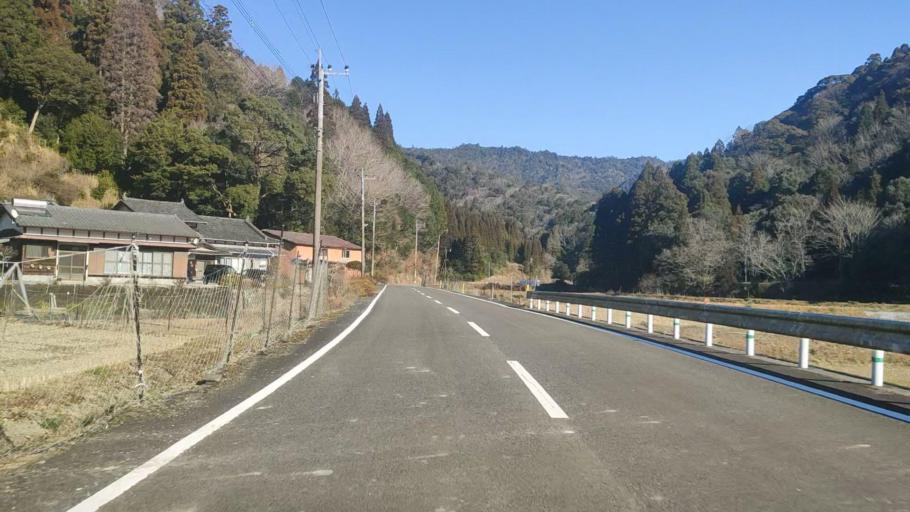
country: JP
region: Oita
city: Saiki
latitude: 32.7762
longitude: 131.8297
